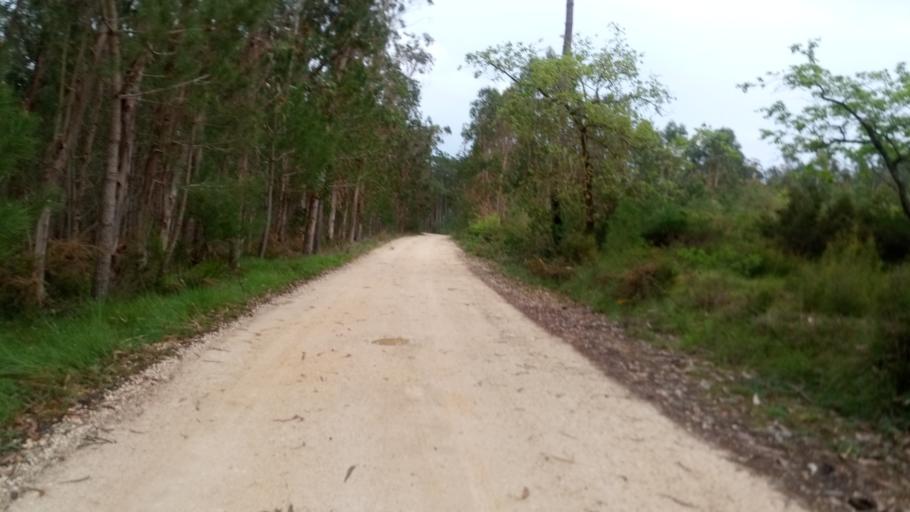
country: PT
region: Leiria
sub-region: Caldas da Rainha
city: Caldas da Rainha
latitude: 39.4546
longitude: -9.1587
